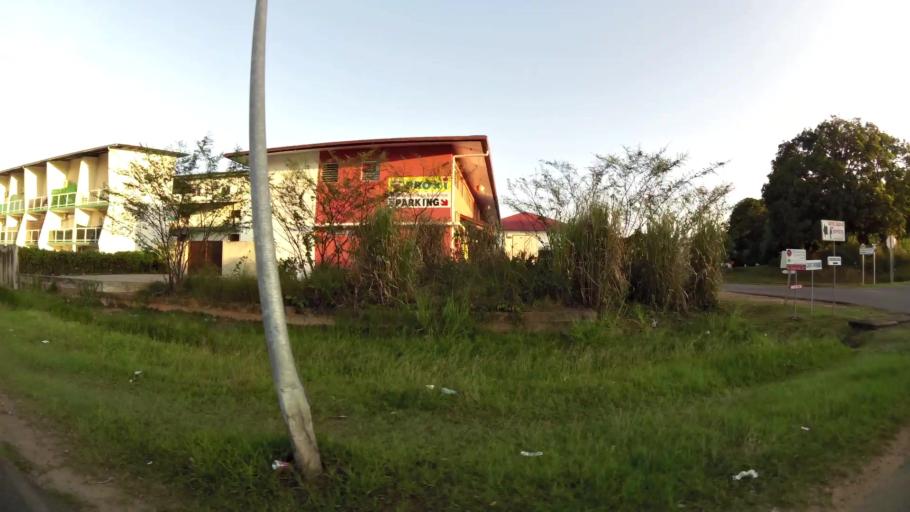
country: GF
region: Guyane
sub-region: Guyane
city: Cayenne
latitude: 4.9270
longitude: -52.3034
